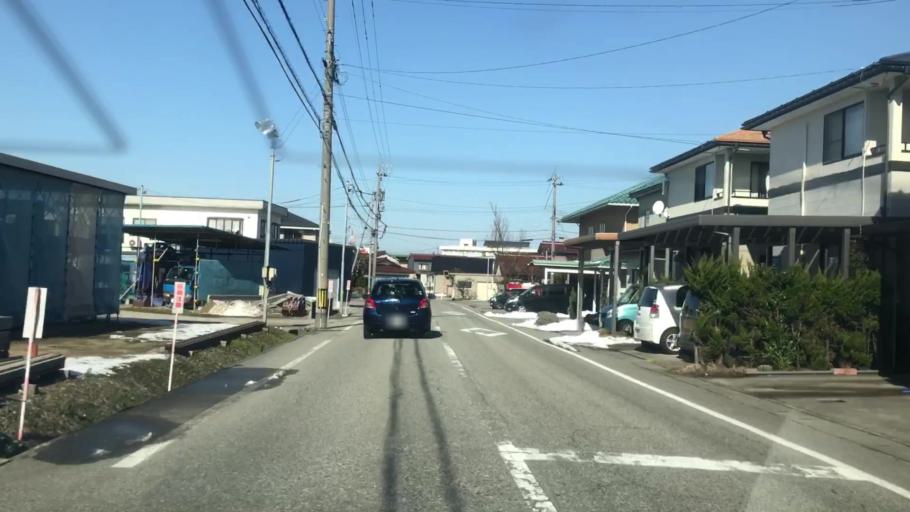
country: JP
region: Toyama
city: Toyama-shi
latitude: 36.6651
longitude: 137.2401
